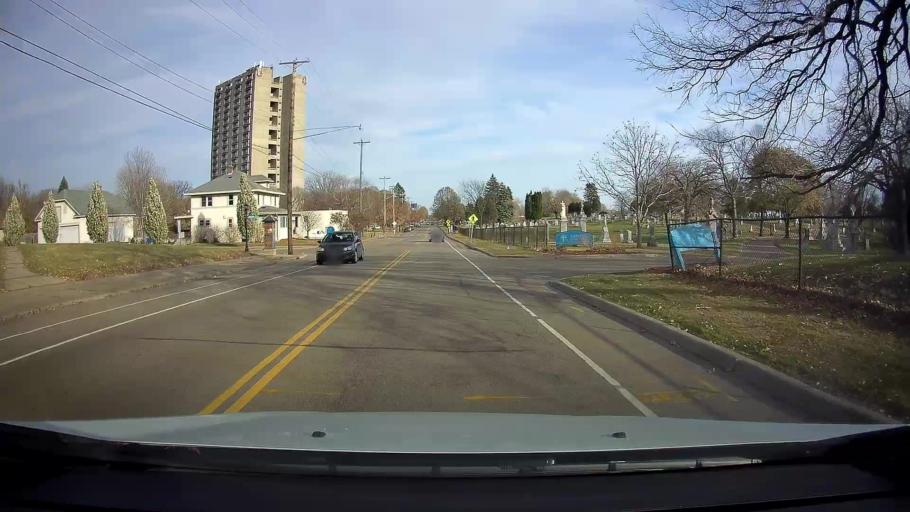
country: US
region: Minnesota
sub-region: Ramsey County
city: Falcon Heights
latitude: 44.9702
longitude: -93.1329
